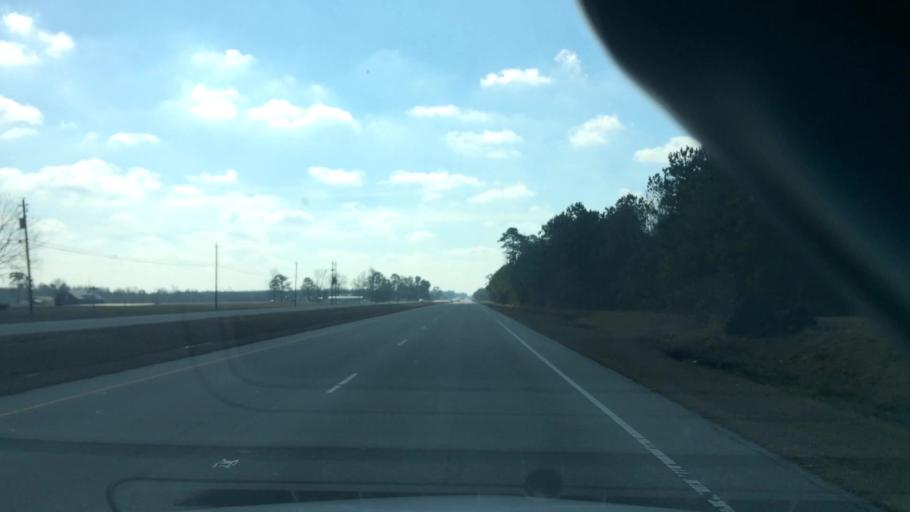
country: US
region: North Carolina
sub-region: Duplin County
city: Beulaville
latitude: 35.1153
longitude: -77.7170
